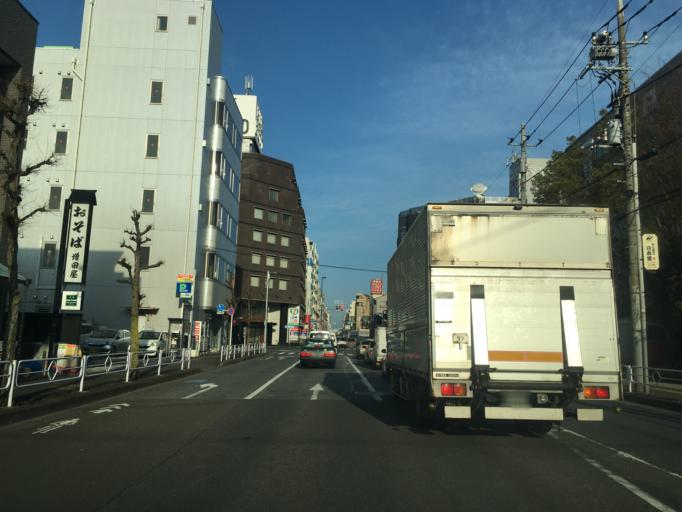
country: JP
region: Tokyo
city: Hino
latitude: 35.6932
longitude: 139.4192
